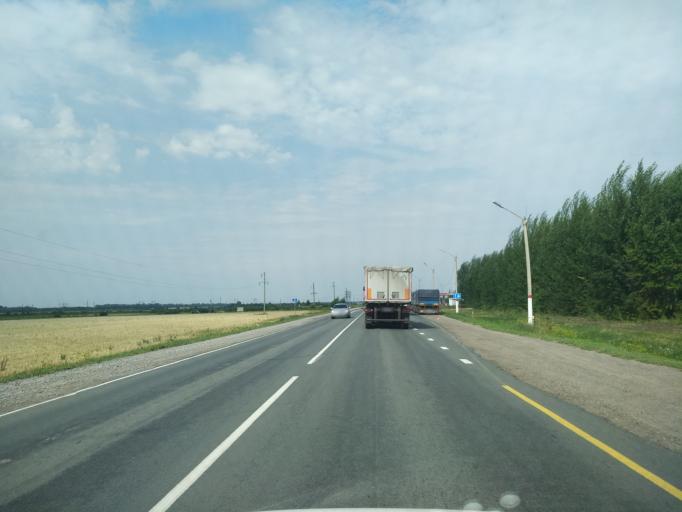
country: RU
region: Voronezj
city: Orlovo
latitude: 51.6774
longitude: 39.6859
